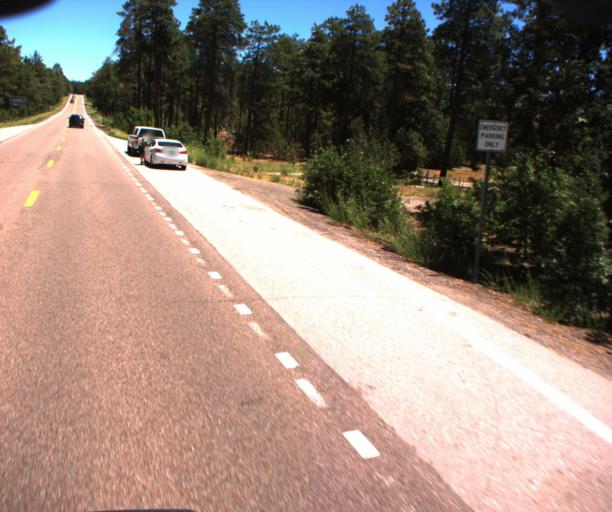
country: US
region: Arizona
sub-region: Gila County
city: Pine
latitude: 34.4366
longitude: -111.5000
